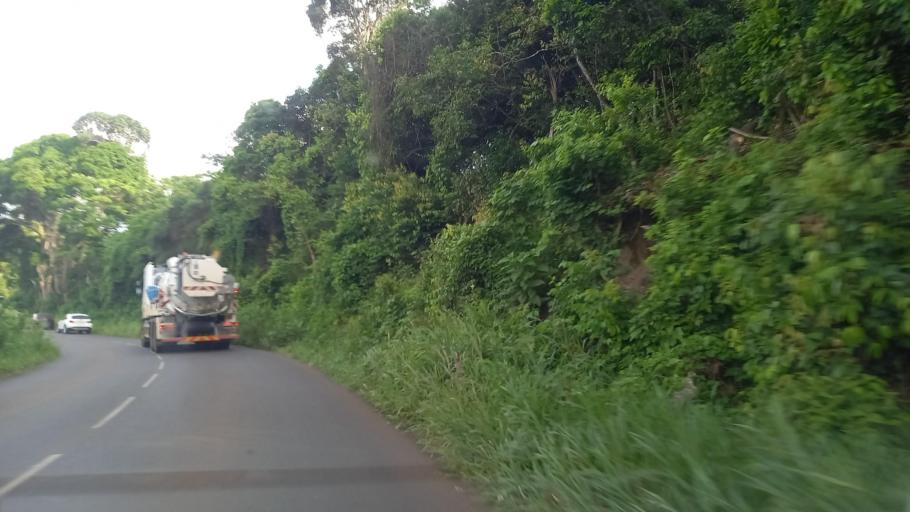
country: YT
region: Chiconi
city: Chiconi
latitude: -12.8124
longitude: 45.1268
